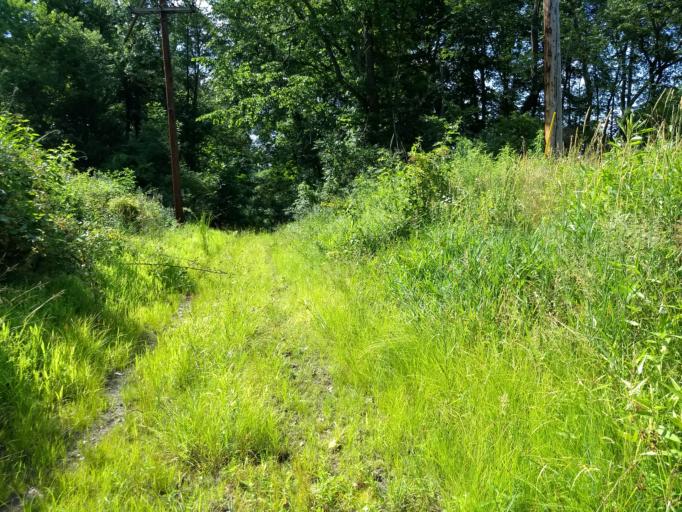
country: US
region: Pennsylvania
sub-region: Westmoreland County
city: Irwin
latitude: 40.3377
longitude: -79.7231
